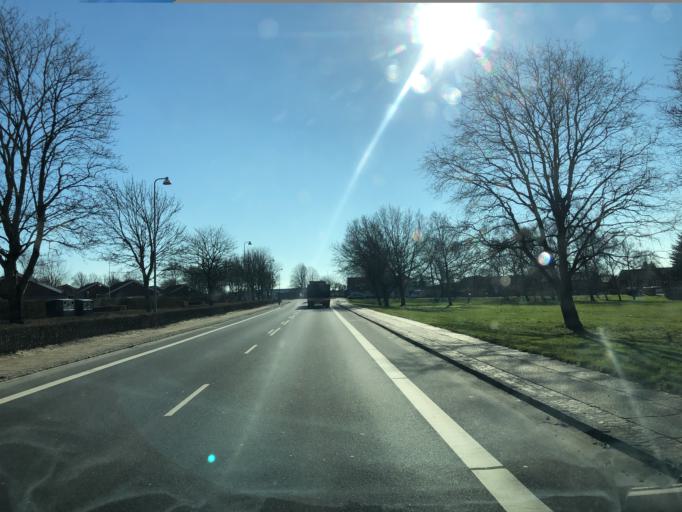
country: DK
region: Central Jutland
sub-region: Ikast-Brande Kommune
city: Ikast
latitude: 56.1342
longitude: 9.1655
